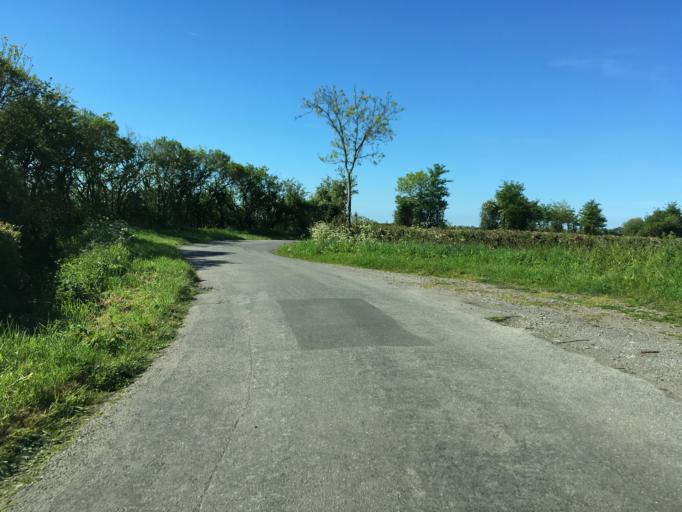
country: GB
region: England
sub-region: South Gloucestershire
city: Severn Beach
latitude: 51.5775
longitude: -2.6278
